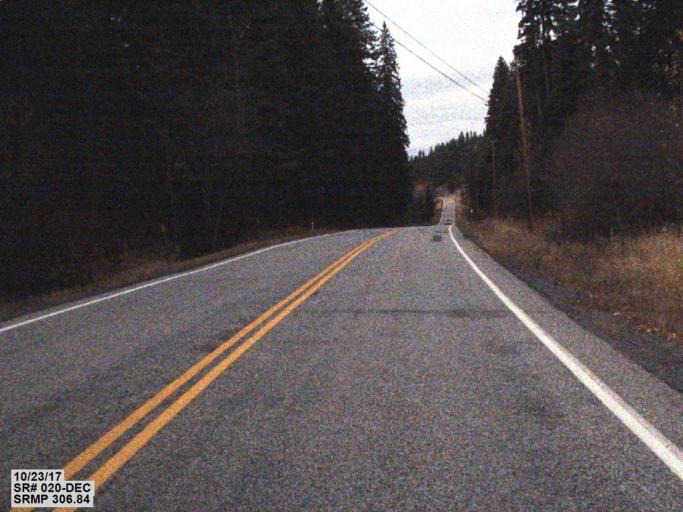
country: US
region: Washington
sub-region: Ferry County
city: Republic
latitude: 48.6296
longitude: -118.6765
